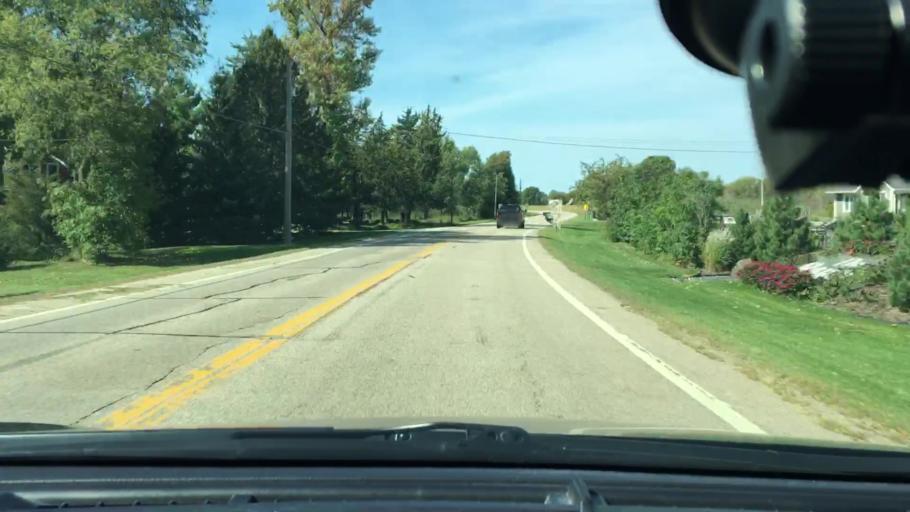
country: US
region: Minnesota
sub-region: Wright County
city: Hanover
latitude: 45.1228
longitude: -93.6161
